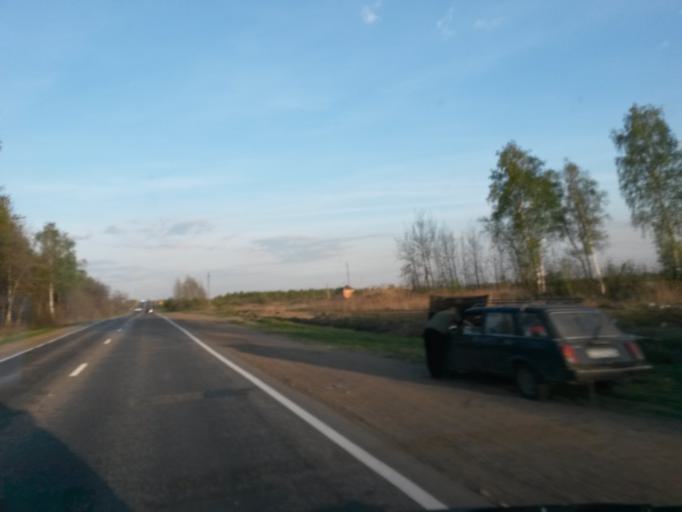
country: RU
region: Jaroslavl
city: Krasnyye Tkachi
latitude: 57.6626
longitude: 39.6952
